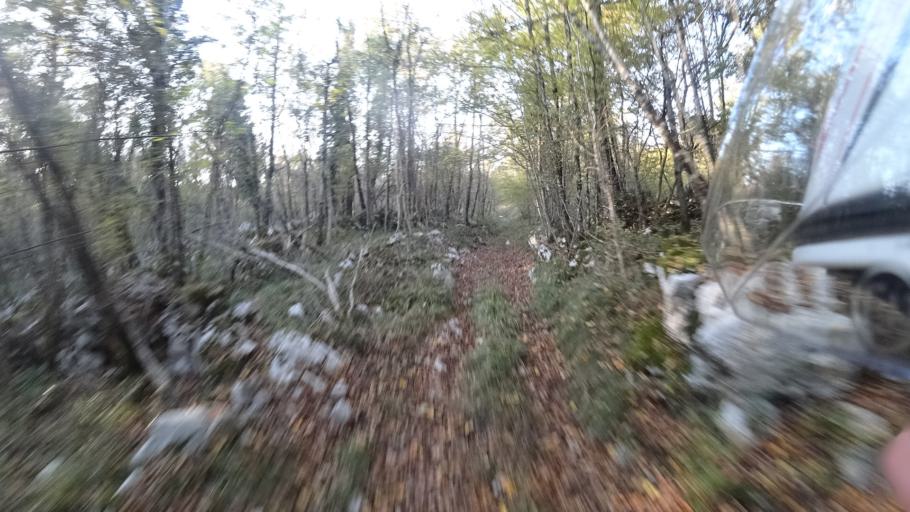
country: HR
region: Primorsko-Goranska
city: Kastav
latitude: 45.4117
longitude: 14.3162
